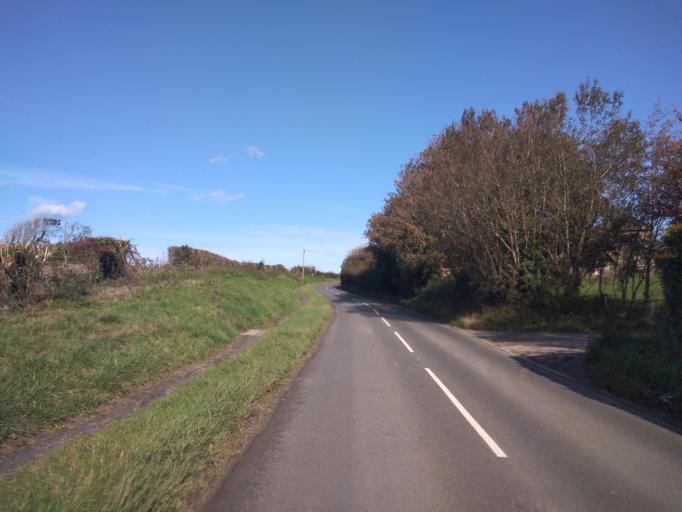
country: GB
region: England
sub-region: East Sussex
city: Seaford
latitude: 50.8214
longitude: 0.1627
